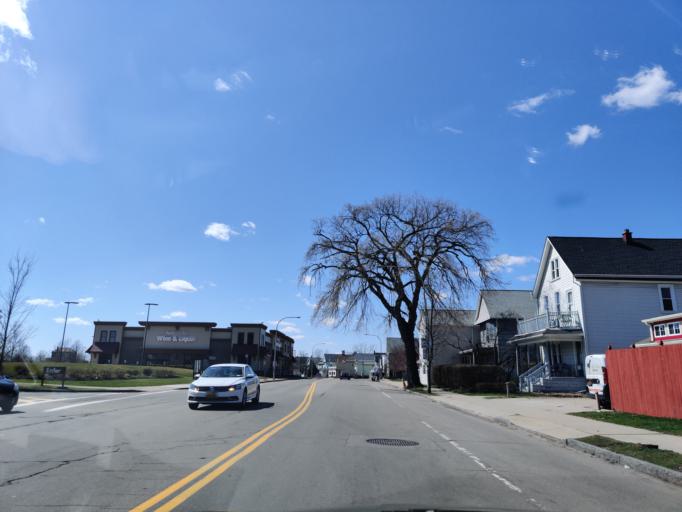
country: US
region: New York
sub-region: Erie County
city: Kenmore
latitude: 42.9406
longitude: -78.8811
